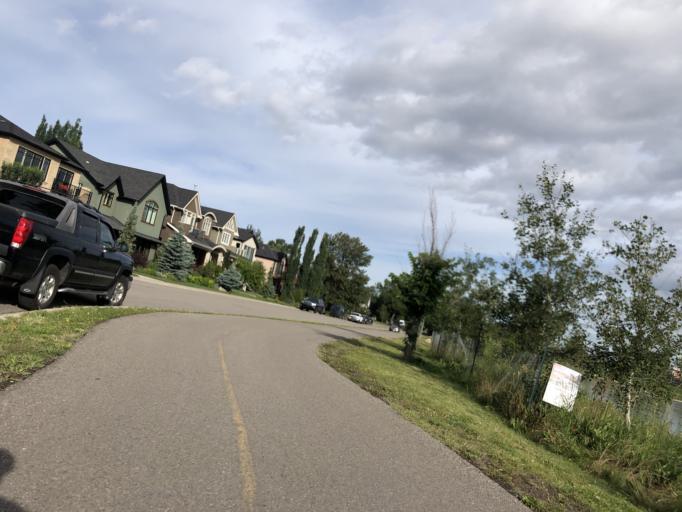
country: CA
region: Alberta
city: Calgary
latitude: 51.0326
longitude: -114.0111
